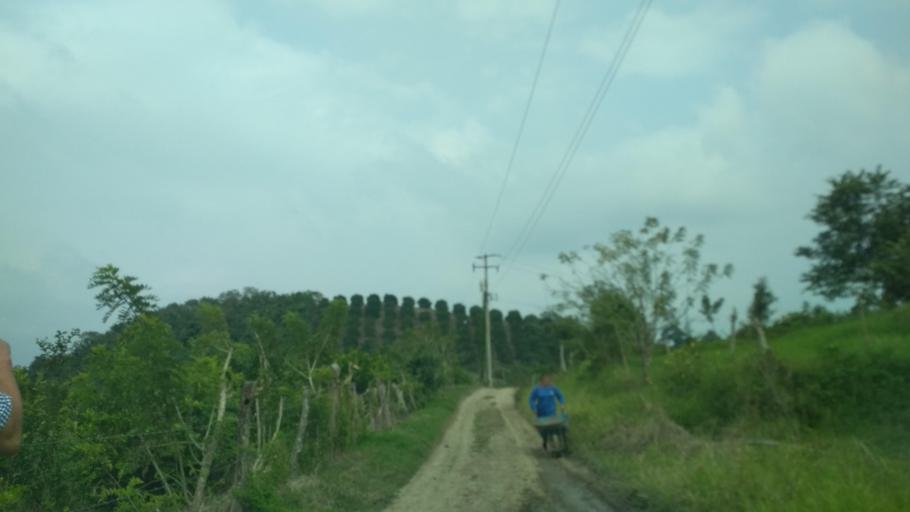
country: MM
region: Kayah
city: Loikaw
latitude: 20.2127
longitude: 97.3153
